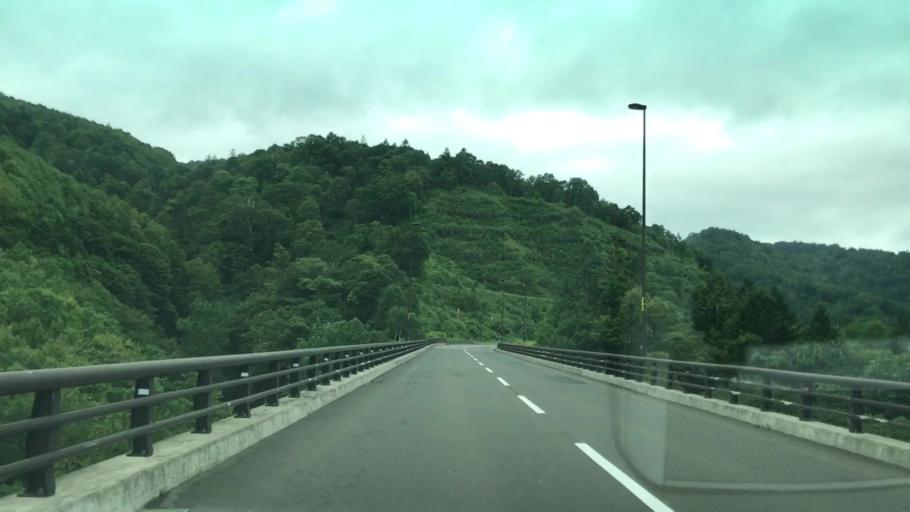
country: JP
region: Hokkaido
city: Otaru
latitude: 42.9925
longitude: 140.8764
